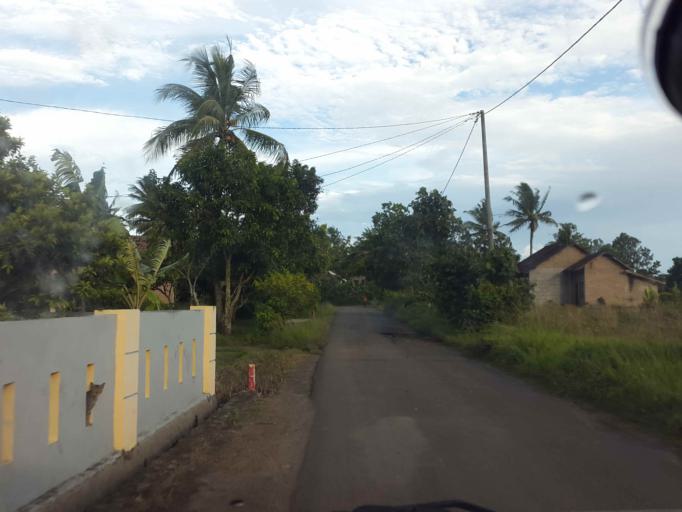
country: ID
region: Lampung
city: Kalianda
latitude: -5.6754
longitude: 105.6054
